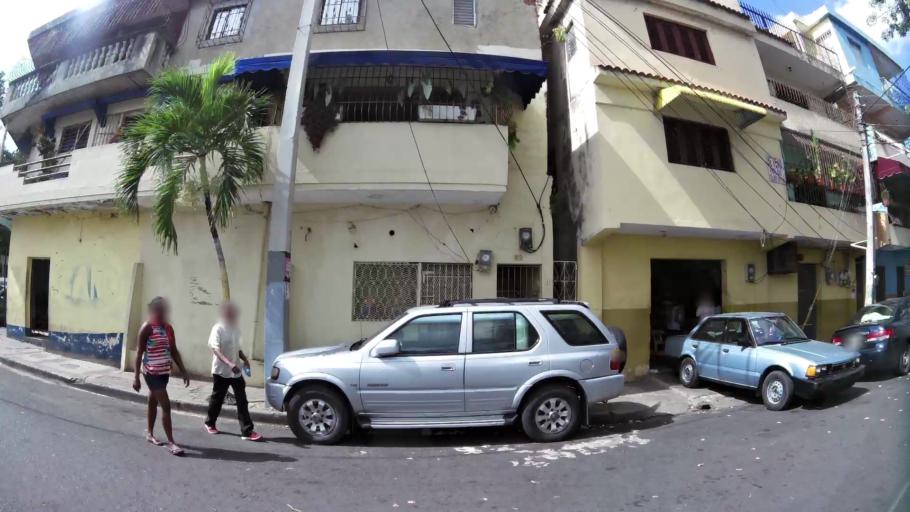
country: DO
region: Nacional
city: San Carlos
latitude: 18.4836
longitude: -69.8968
